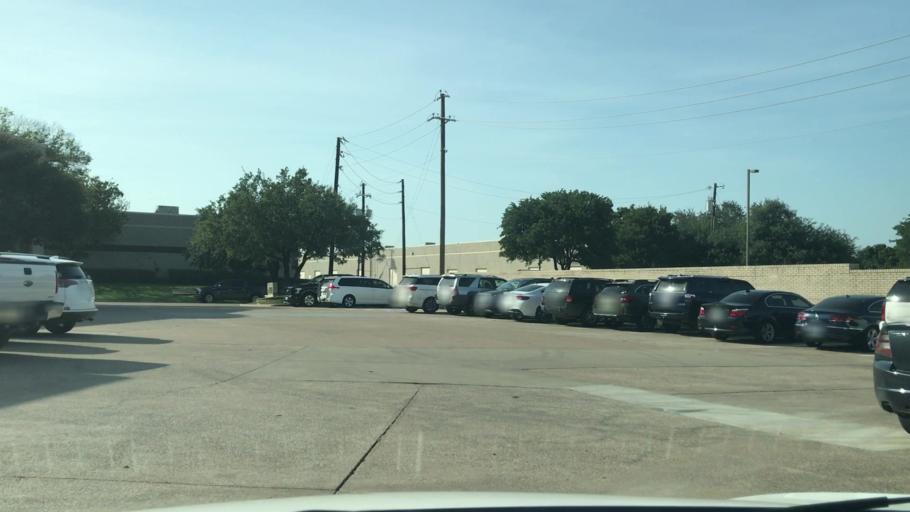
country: US
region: Texas
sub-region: Dallas County
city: Richardson
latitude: 32.8901
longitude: -96.7042
